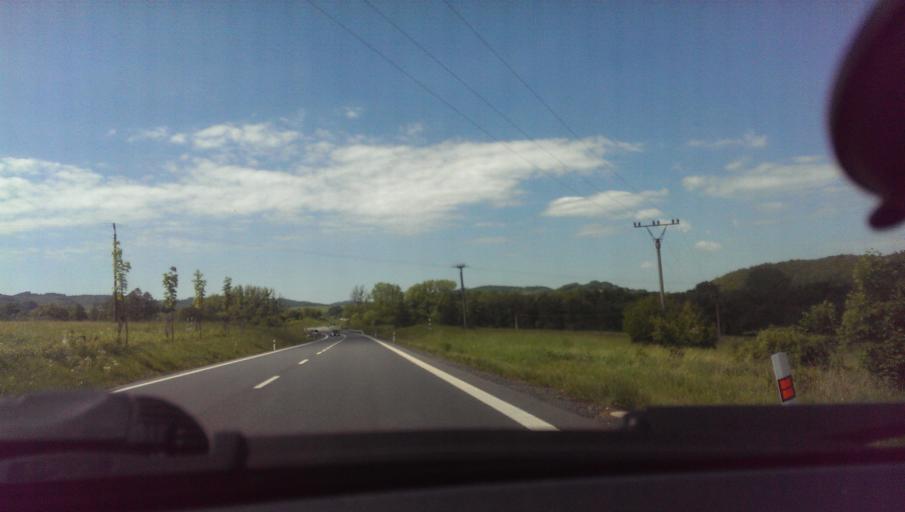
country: CZ
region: Zlin
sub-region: Okres Zlin
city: Vizovice
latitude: 49.2157
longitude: 17.8765
